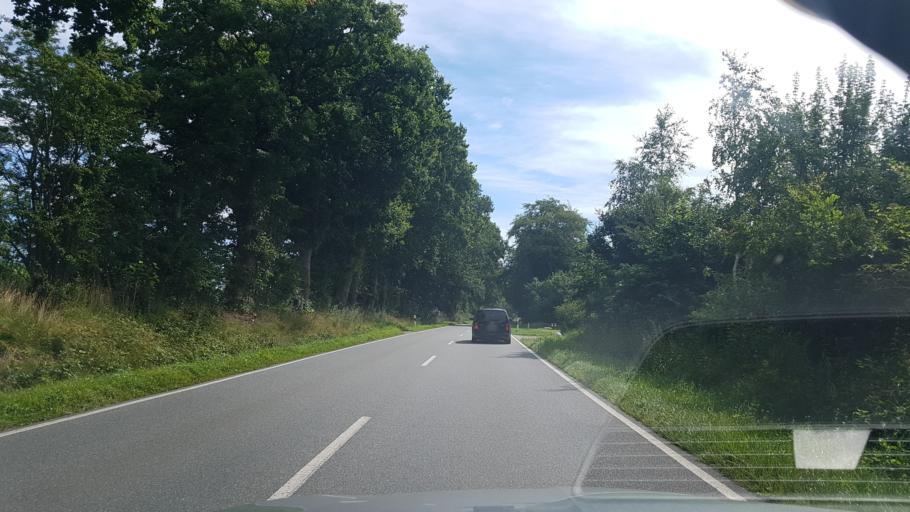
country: DE
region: Schleswig-Holstein
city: Handewitt
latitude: 54.7960
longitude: 9.2941
